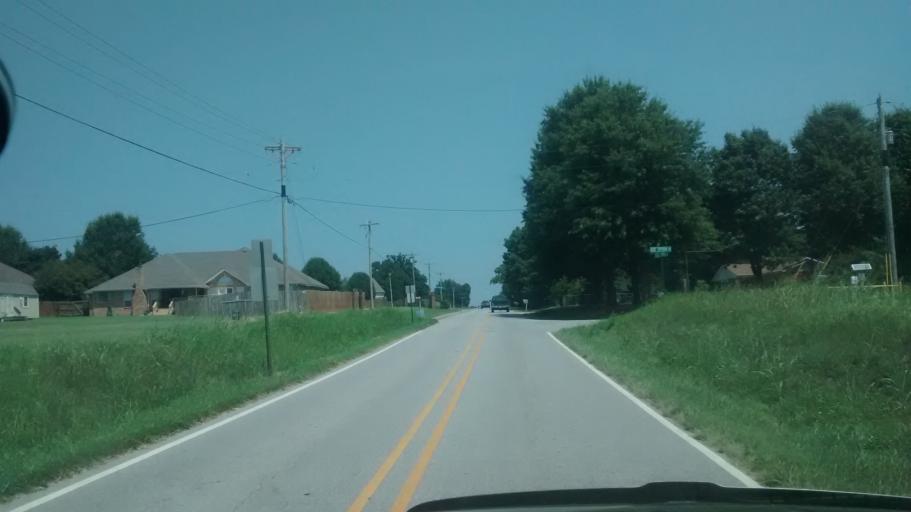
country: US
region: Arkansas
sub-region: Washington County
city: Farmington
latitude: 36.0670
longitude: -94.2535
